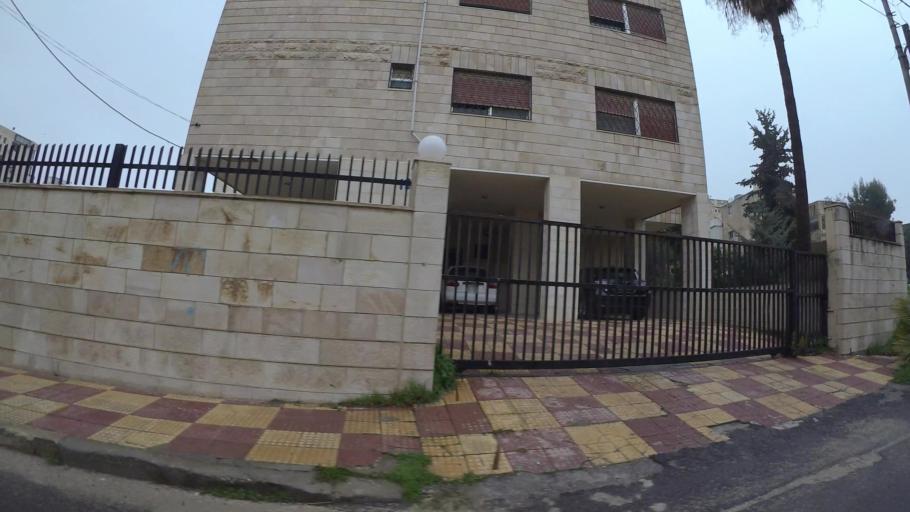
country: JO
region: Amman
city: Wadi as Sir
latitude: 31.9614
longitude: 35.8563
